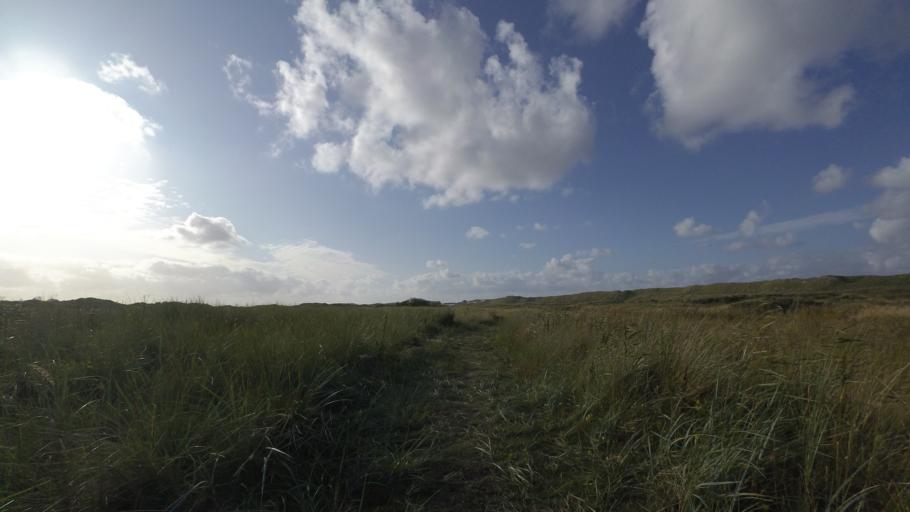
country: NL
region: Friesland
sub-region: Gemeente Dongeradeel
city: Ternaard
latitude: 53.4635
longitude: 5.9155
